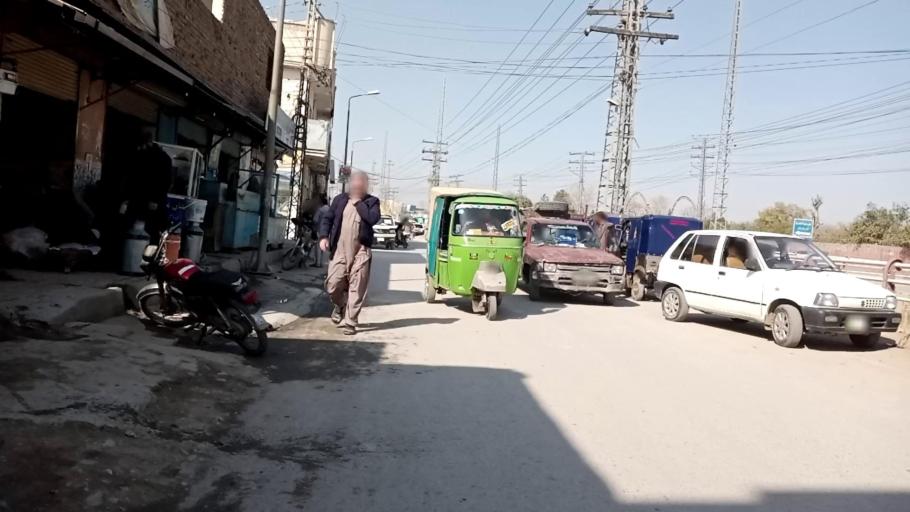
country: PK
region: Khyber Pakhtunkhwa
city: Peshawar
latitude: 33.9928
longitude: 71.4826
